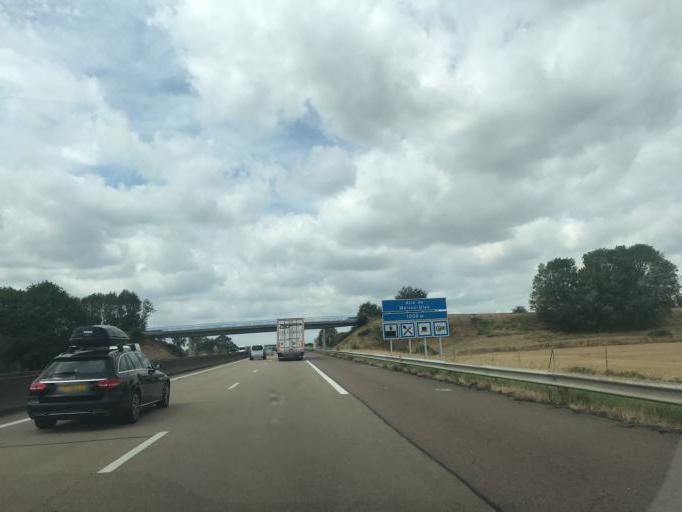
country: FR
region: Bourgogne
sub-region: Departement de l'Yonne
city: Avallon
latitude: 47.5048
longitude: 4.0559
